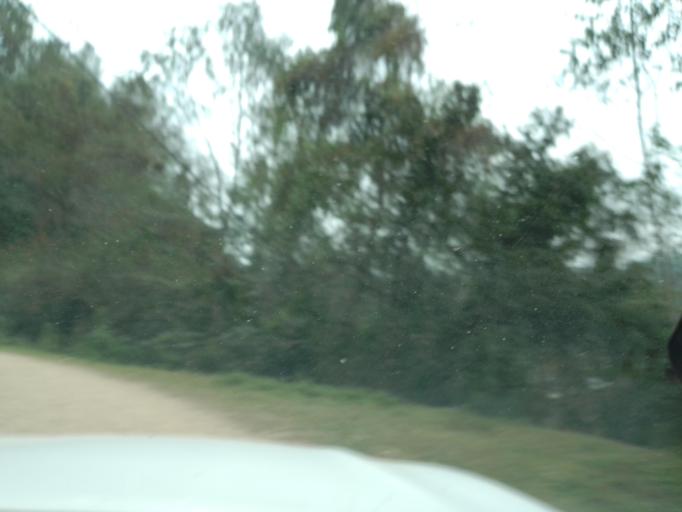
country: MX
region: Chiapas
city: Motozintla de Mendoza
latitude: 15.2208
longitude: -92.2265
